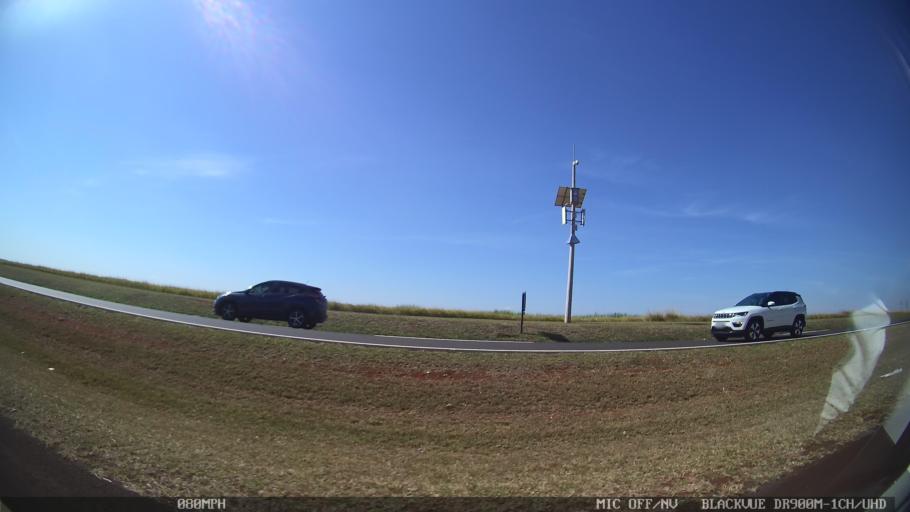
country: BR
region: Sao Paulo
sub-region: Ribeirao Preto
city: Ribeirao Preto
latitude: -21.1822
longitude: -47.8914
